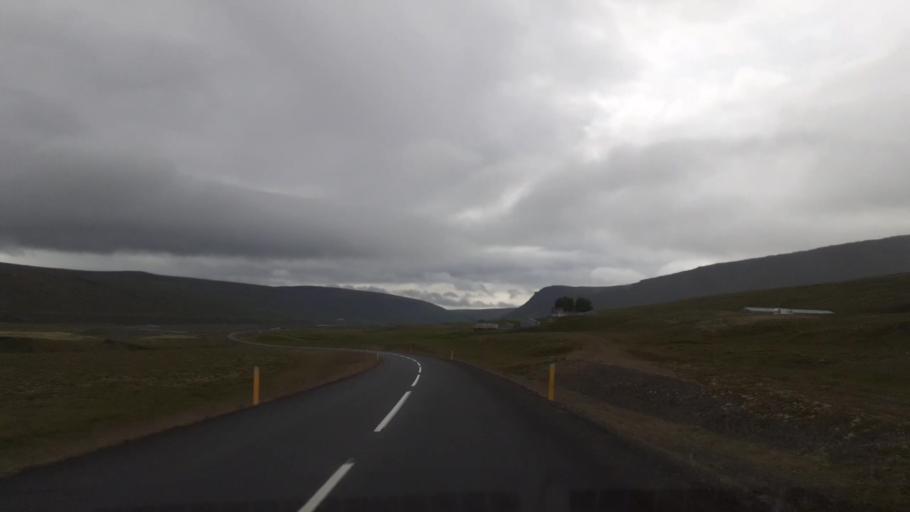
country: IS
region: East
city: Egilsstadir
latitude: 65.6360
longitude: -15.0542
